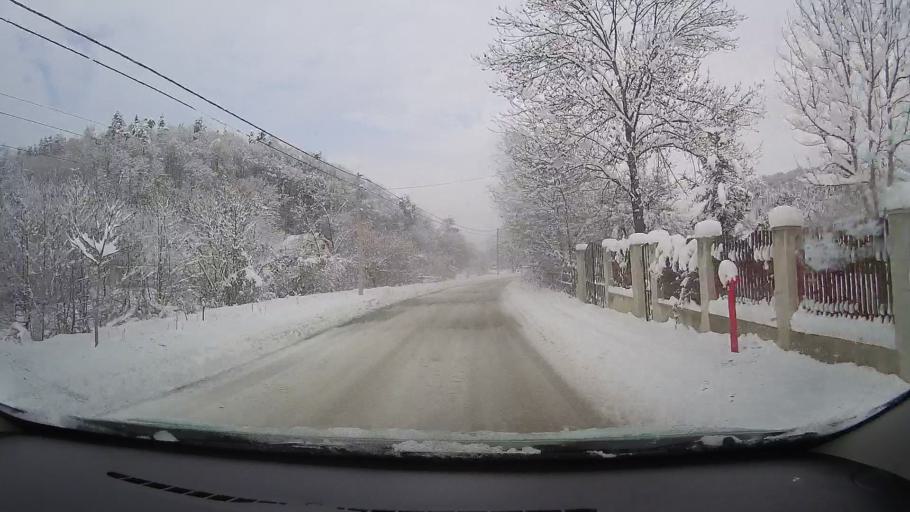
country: RO
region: Alba
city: Pianu de Sus
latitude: 45.8848
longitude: 23.4898
